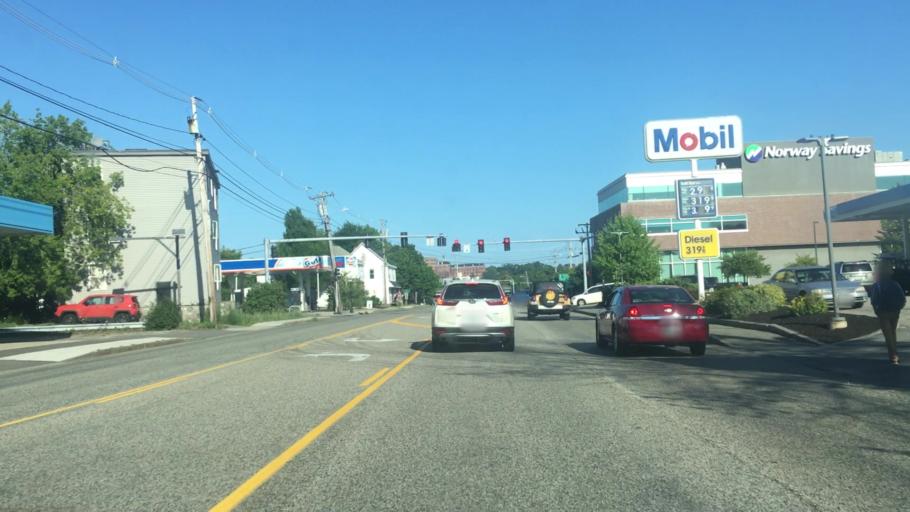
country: US
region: Maine
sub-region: Cumberland County
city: South Portland Gardens
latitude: 43.6573
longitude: -70.2899
